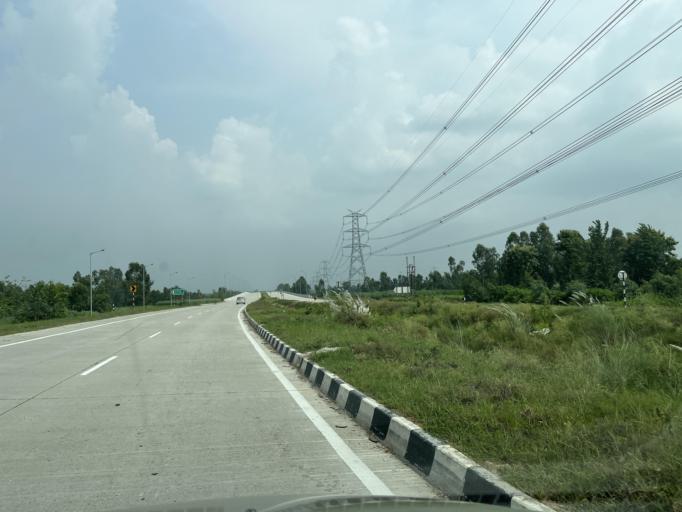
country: IN
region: Uttarakhand
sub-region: Udham Singh Nagar
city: Jaspur
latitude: 29.2978
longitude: 78.8369
